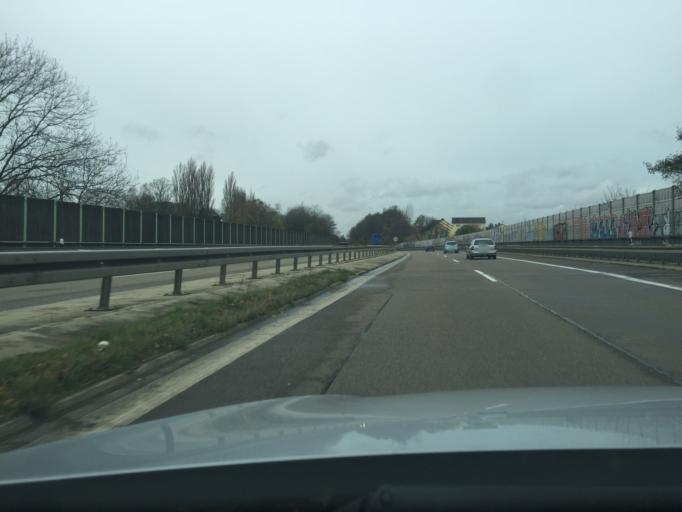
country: DE
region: North Rhine-Westphalia
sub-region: Regierungsbezirk Dusseldorf
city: Velbert
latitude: 51.3443
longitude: 7.0516
